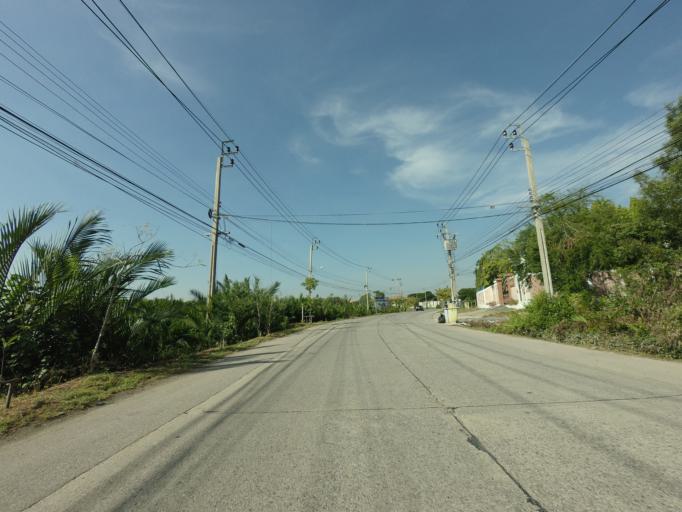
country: TH
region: Samut Prakan
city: Phra Samut Chedi
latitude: 13.5673
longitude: 100.5552
